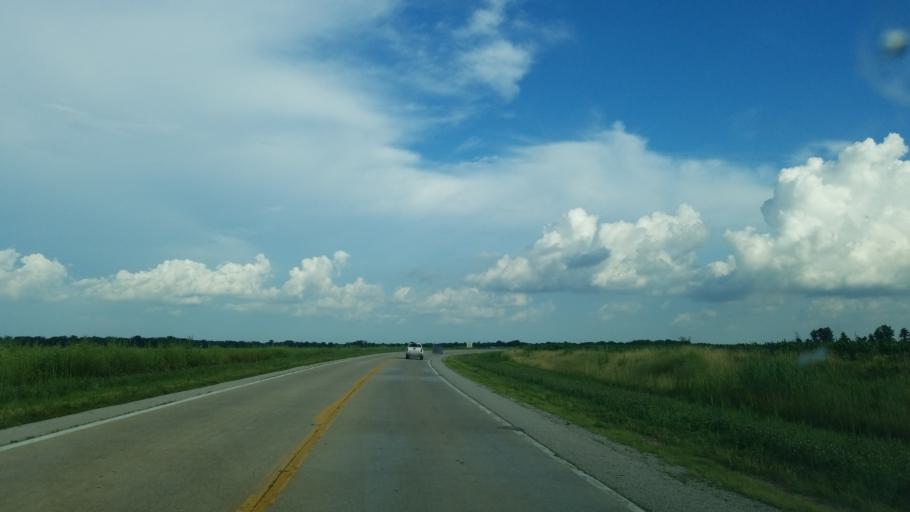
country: US
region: Illinois
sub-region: Marion County
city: Sandoval
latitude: 38.6036
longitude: -89.1109
